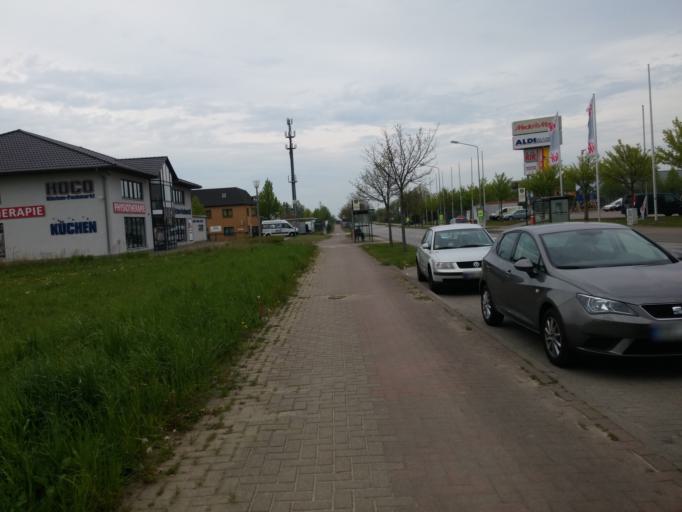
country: DE
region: Mecklenburg-Vorpommern
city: Roggentin
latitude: 54.0826
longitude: 12.1934
